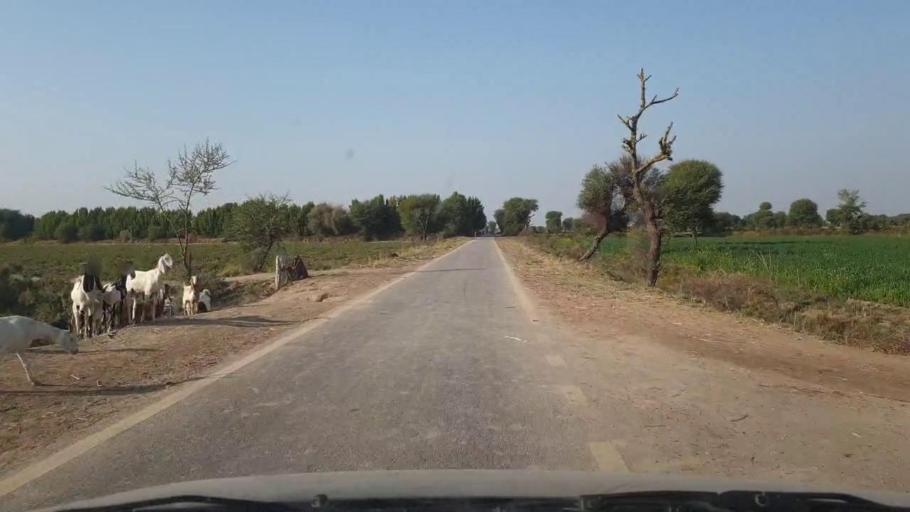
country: PK
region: Sindh
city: Samaro
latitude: 25.2971
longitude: 69.3486
